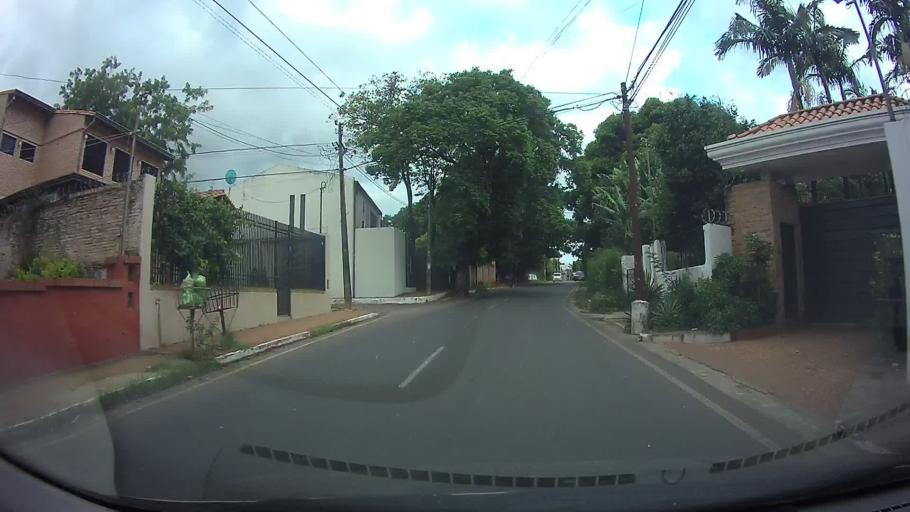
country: PY
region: Central
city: Fernando de la Mora
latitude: -25.3137
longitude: -57.5515
